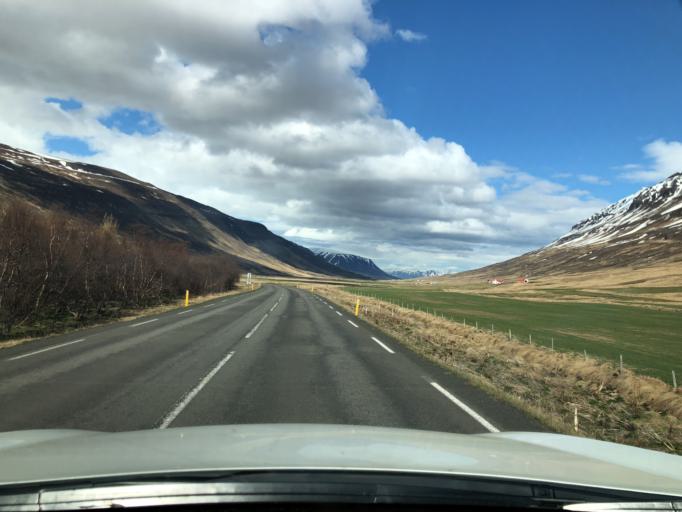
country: IS
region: Northeast
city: Dalvik
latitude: 65.6041
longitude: -18.5085
